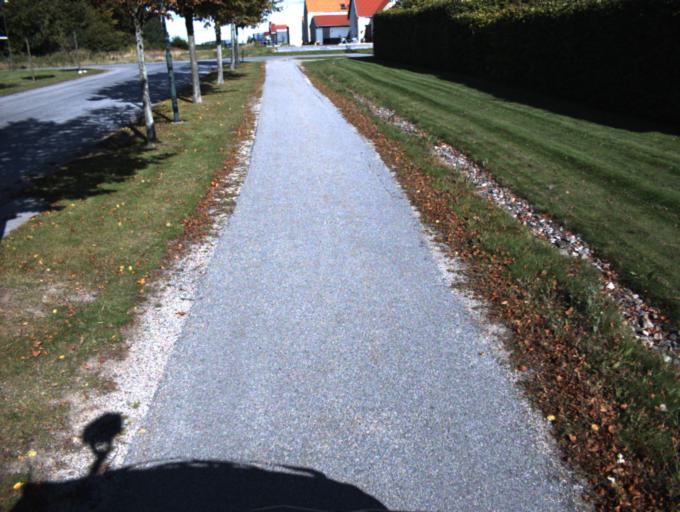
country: SE
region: Skane
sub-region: Helsingborg
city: Helsingborg
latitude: 56.0874
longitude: 12.6899
